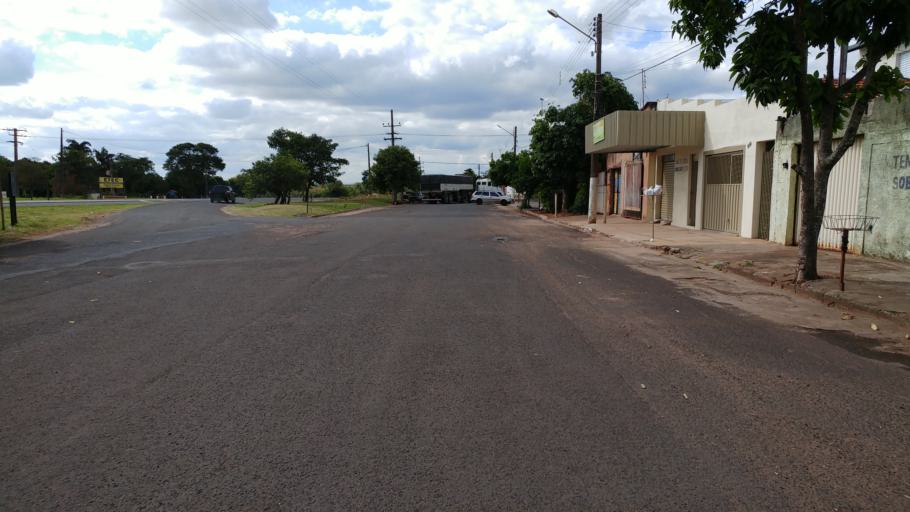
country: BR
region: Sao Paulo
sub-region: Paraguacu Paulista
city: Paraguacu Paulista
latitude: -22.4174
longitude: -50.5932
